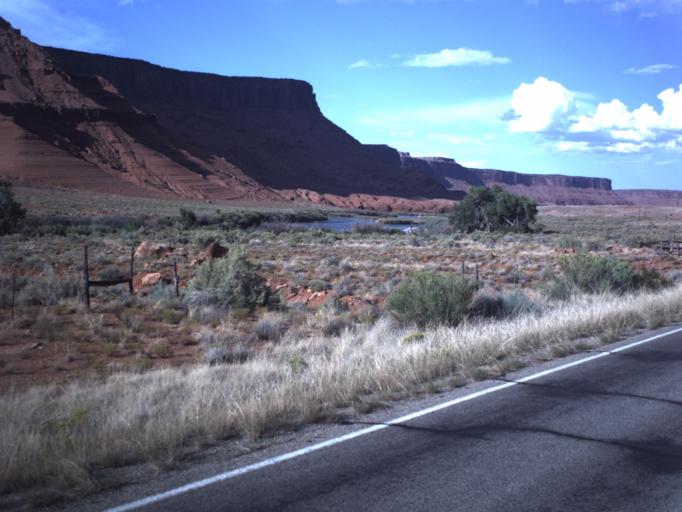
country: US
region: Utah
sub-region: Grand County
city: Moab
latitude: 38.6834
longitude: -109.4233
